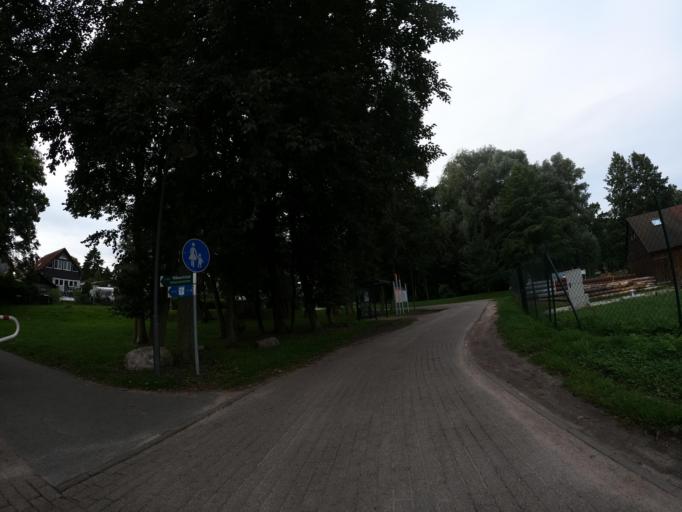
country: DE
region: Mecklenburg-Vorpommern
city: Malchow
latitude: 53.4913
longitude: 12.4804
